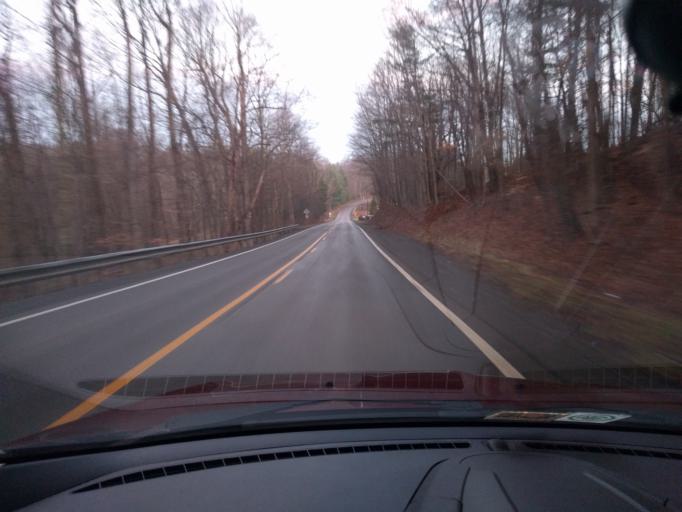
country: US
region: West Virginia
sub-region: Greenbrier County
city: Rainelle
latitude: 37.9985
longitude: -80.8767
